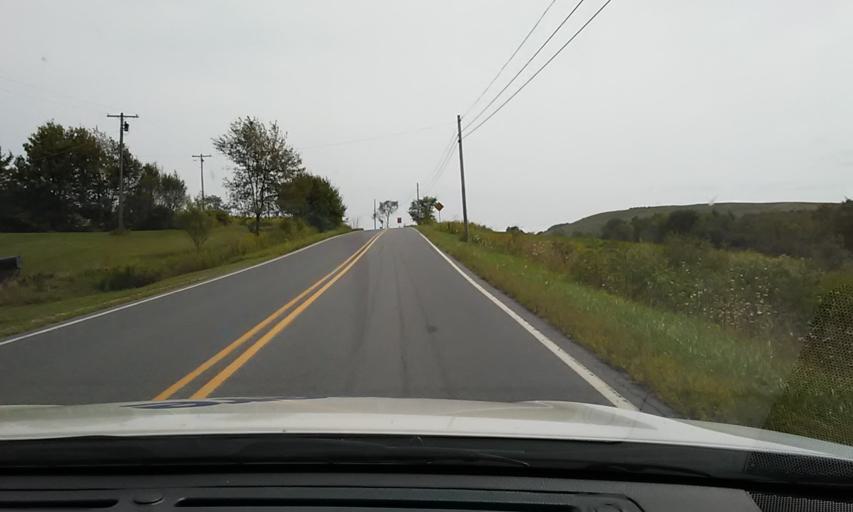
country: US
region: Pennsylvania
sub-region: Elk County
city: Ridgway
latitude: 41.3131
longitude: -78.6543
